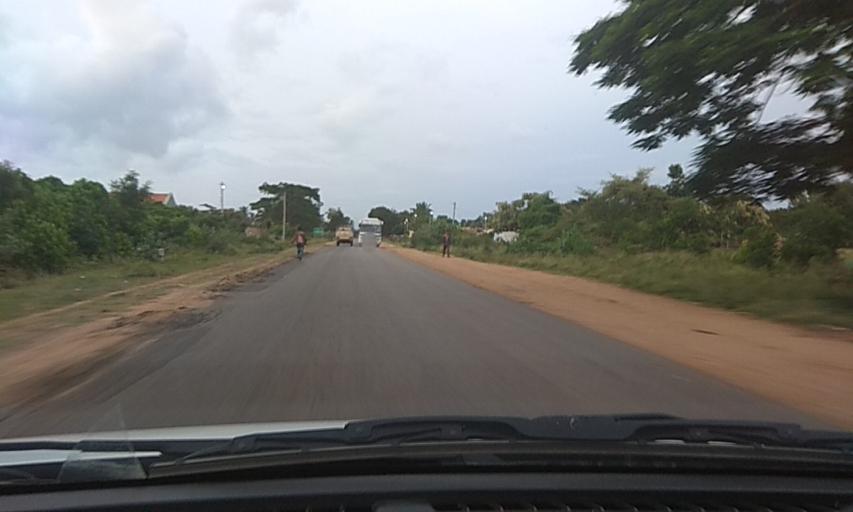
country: IN
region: Karnataka
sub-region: Chamrajnagar
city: Gundlupet
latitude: 11.8110
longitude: 76.7346
